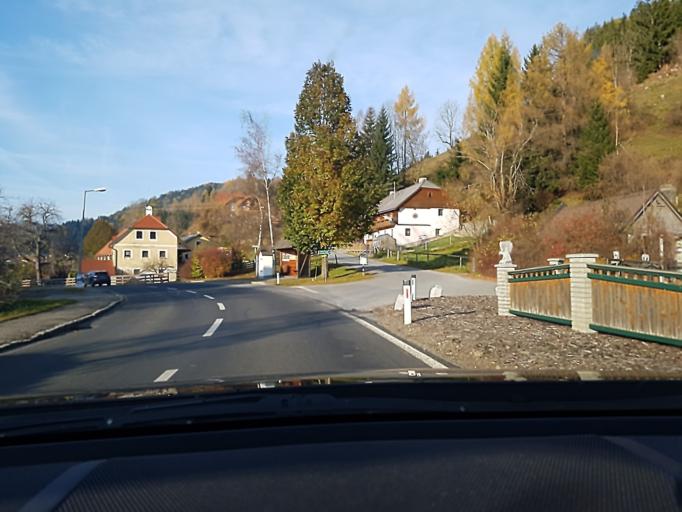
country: AT
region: Styria
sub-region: Politischer Bezirk Murau
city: Oberwolz Stadt
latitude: 47.2044
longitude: 14.2549
